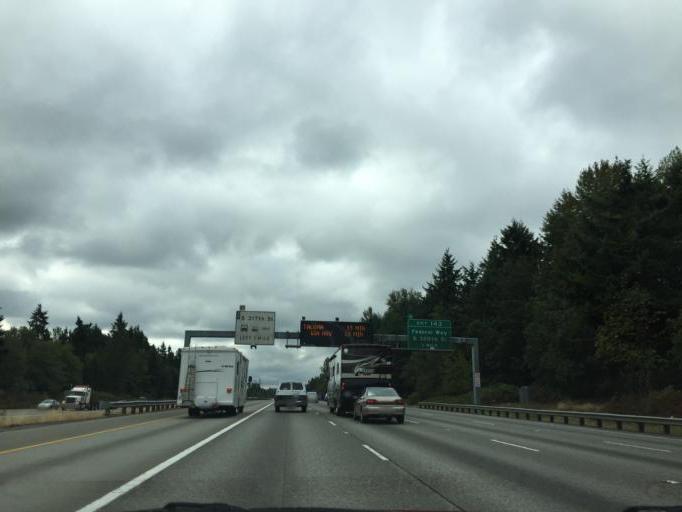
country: US
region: Washington
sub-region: King County
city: Lakeland North
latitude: 47.3354
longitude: -122.2937
